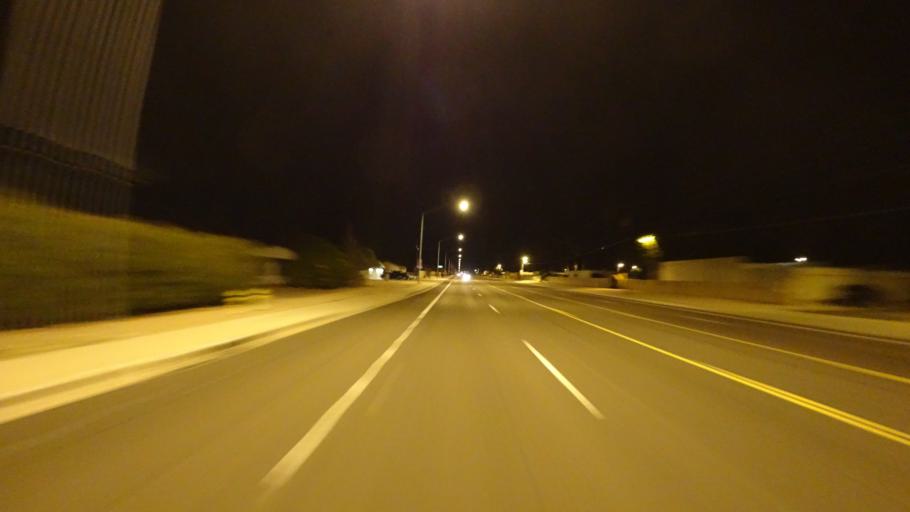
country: US
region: Arizona
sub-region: Maricopa County
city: Mesa
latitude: 33.4540
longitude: -111.7015
